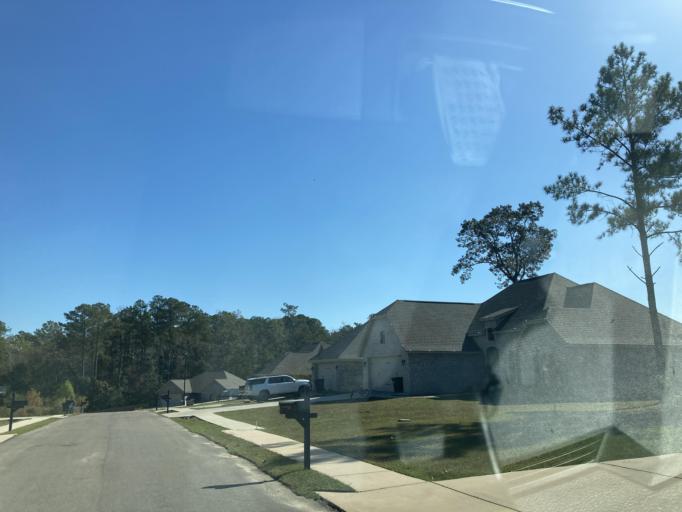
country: US
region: Mississippi
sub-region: Lamar County
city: West Hattiesburg
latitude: 31.2805
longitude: -89.4087
